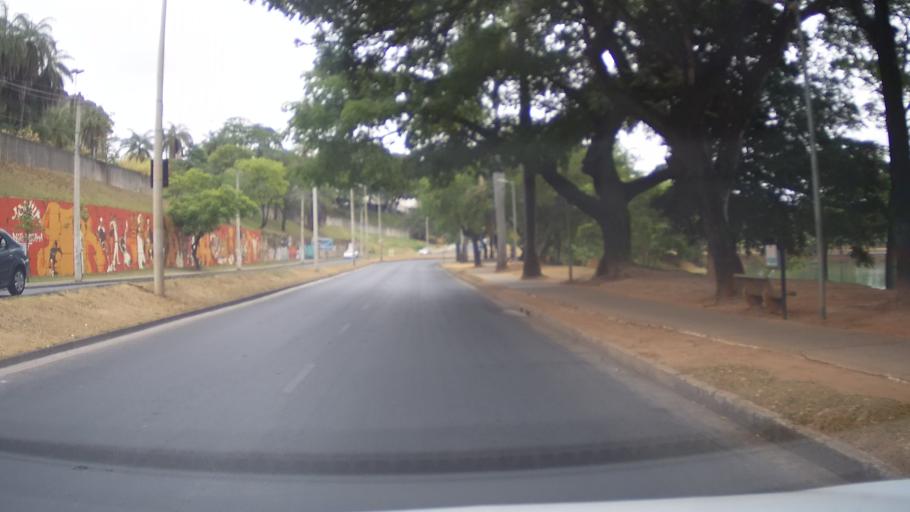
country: BR
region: Minas Gerais
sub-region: Belo Horizonte
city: Belo Horizonte
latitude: -19.8611
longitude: -43.9750
